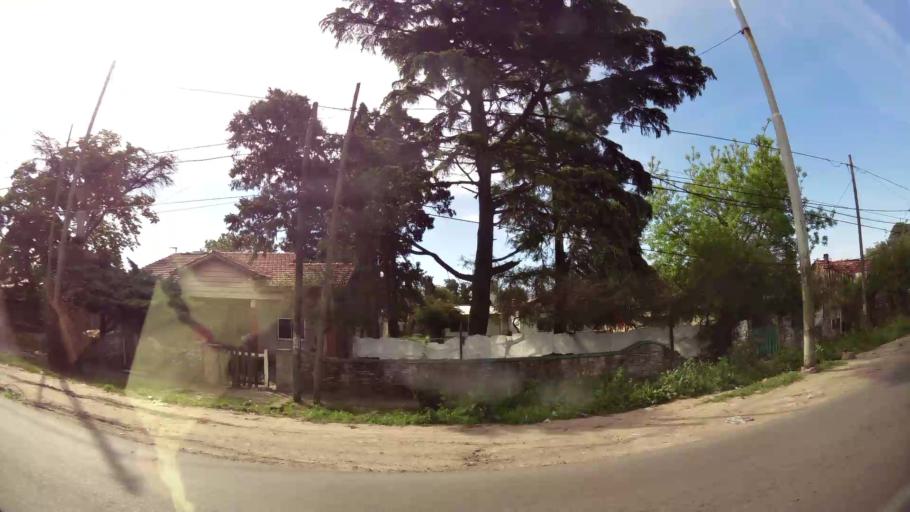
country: AR
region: Buenos Aires
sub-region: Partido de Almirante Brown
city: Adrogue
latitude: -34.8092
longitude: -58.3443
